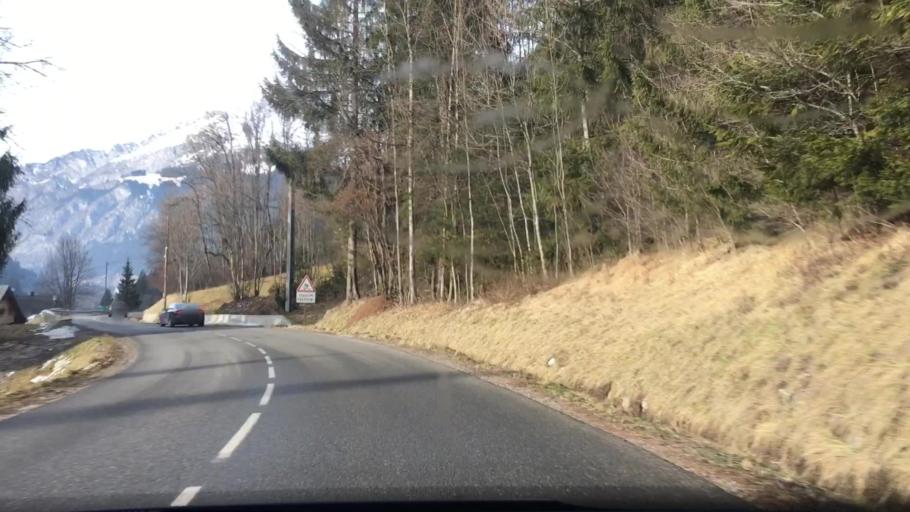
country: FR
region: Rhone-Alpes
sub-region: Departement de la Haute-Savoie
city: Chatel
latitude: 46.2797
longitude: 6.8260
